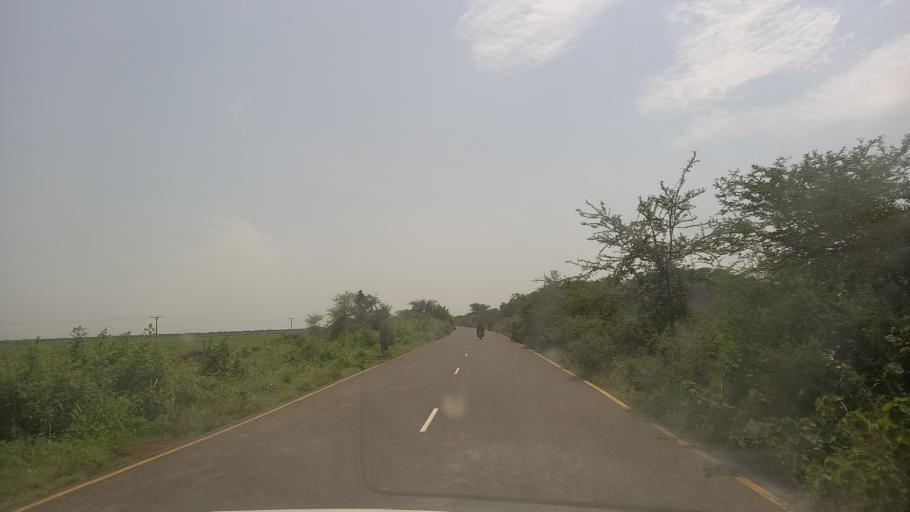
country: ET
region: Gambela
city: Gambela
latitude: 8.2832
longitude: 34.2183
